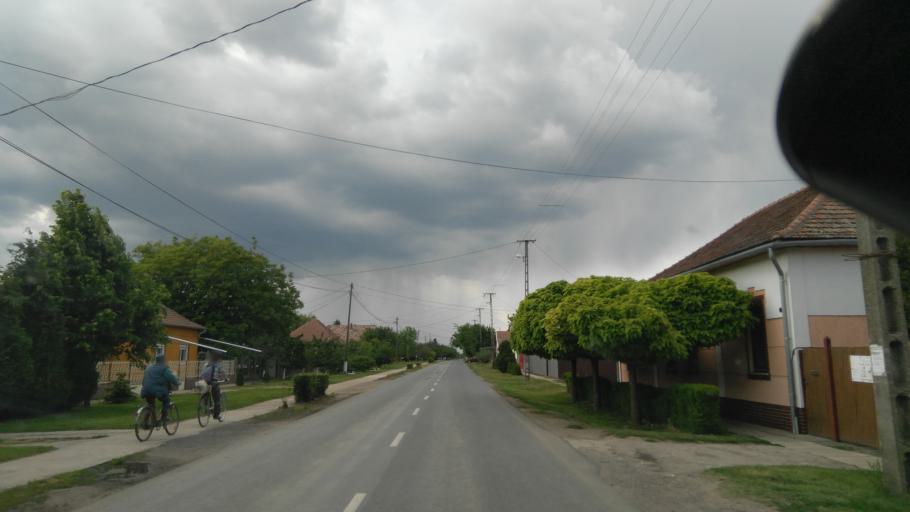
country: HU
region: Bekes
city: Dombegyhaz
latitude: 46.3445
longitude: 21.1260
